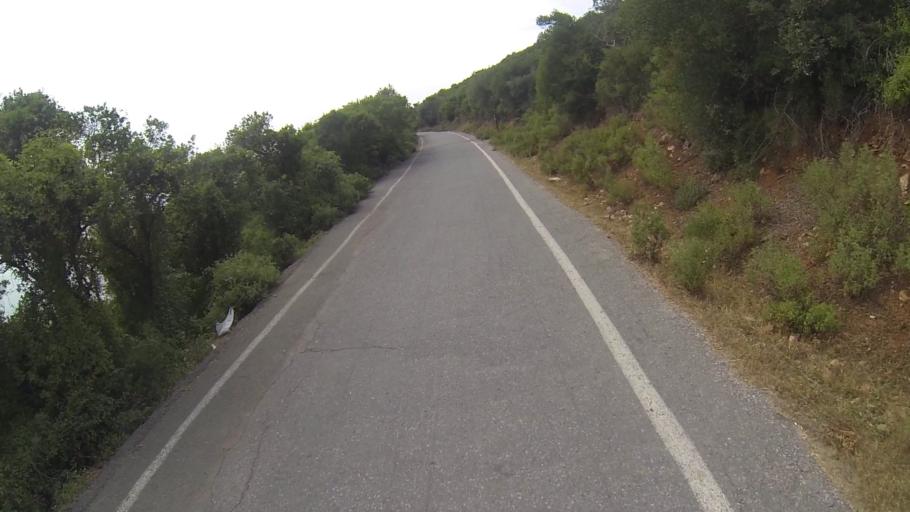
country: TR
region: Istanbul
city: Adalar
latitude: 40.8393
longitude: 29.1186
